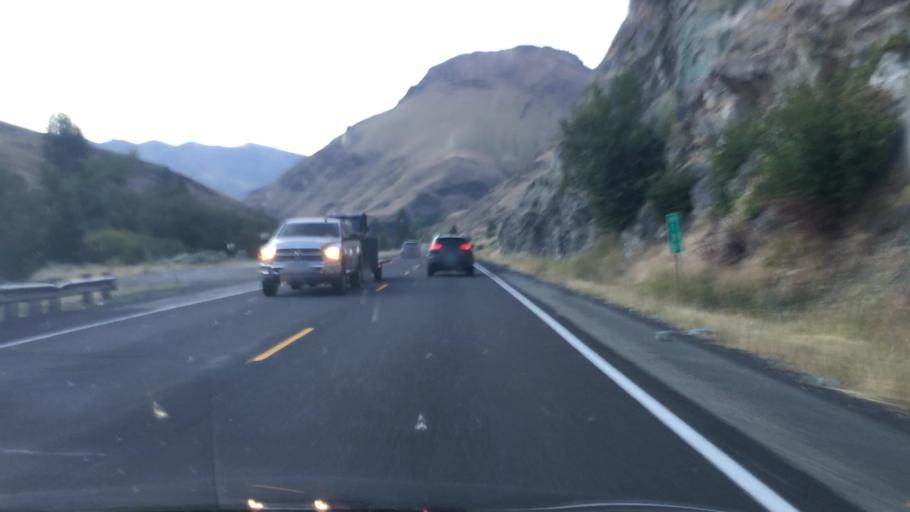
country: US
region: Idaho
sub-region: Valley County
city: McCall
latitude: 45.3307
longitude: -116.3472
